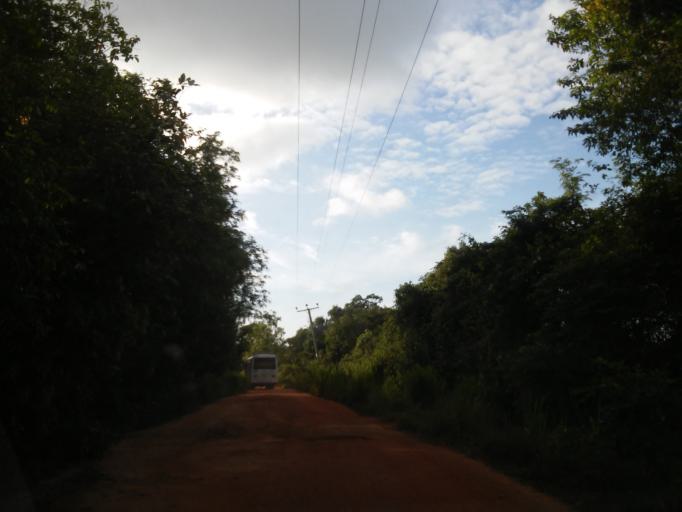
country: LK
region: Central
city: Sigiriya
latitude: 8.1701
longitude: 80.6828
